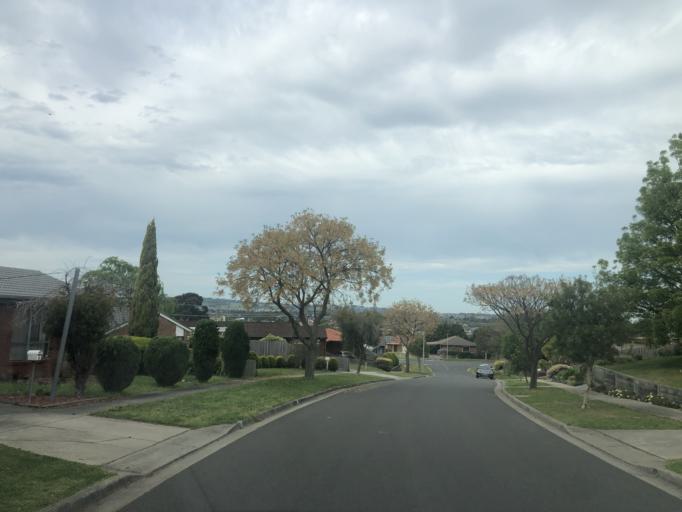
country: AU
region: Victoria
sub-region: Casey
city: Hallam
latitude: -38.0058
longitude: 145.2780
